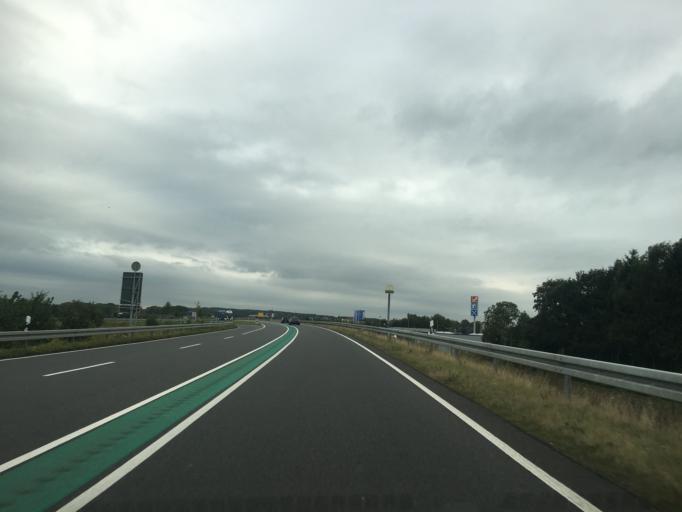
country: DE
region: North Rhine-Westphalia
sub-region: Regierungsbezirk Munster
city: Steinfurt
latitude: 52.1608
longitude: 7.3177
